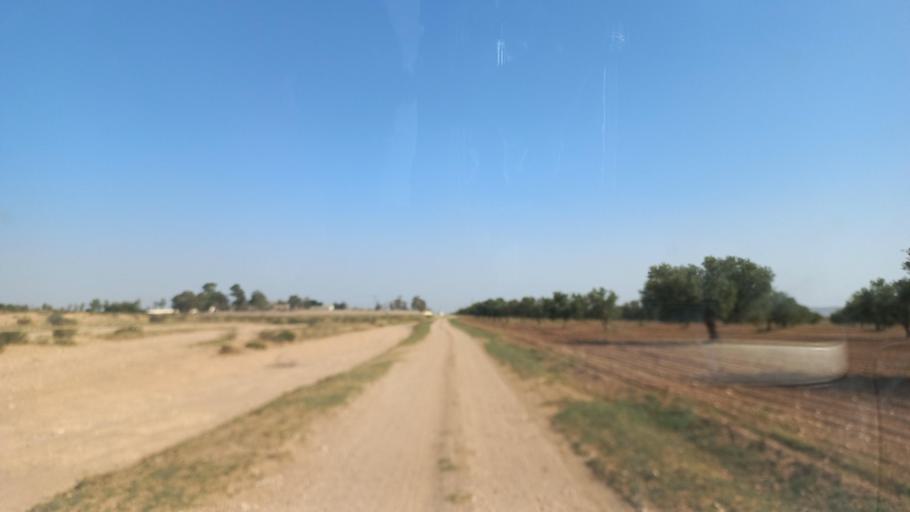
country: TN
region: Al Qasrayn
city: Kasserine
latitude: 35.2993
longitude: 9.0285
